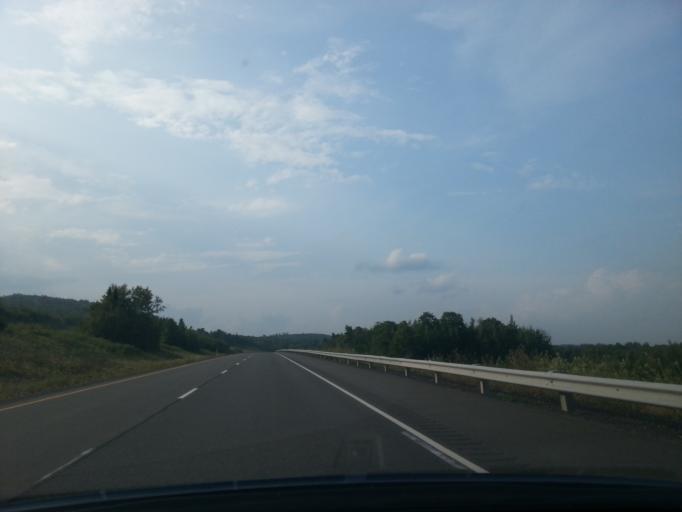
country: US
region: Maine
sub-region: Aroostook County
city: Fort Fairfield
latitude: 46.6910
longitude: -67.7368
